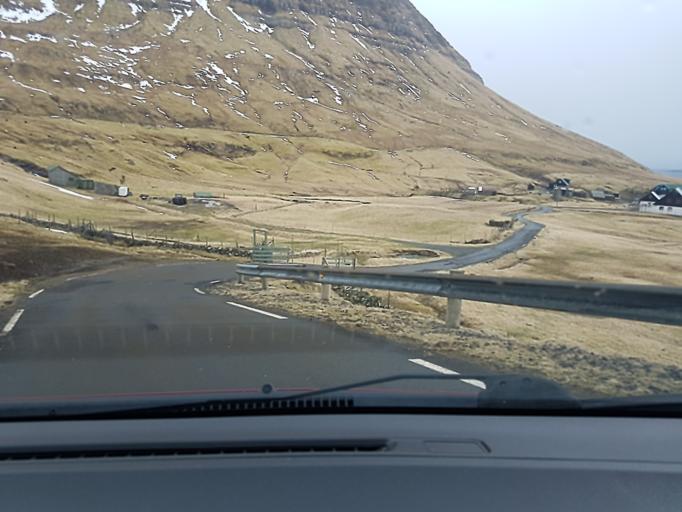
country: FO
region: Streymoy
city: Kollafjordhur
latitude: 62.0424
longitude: -6.9261
